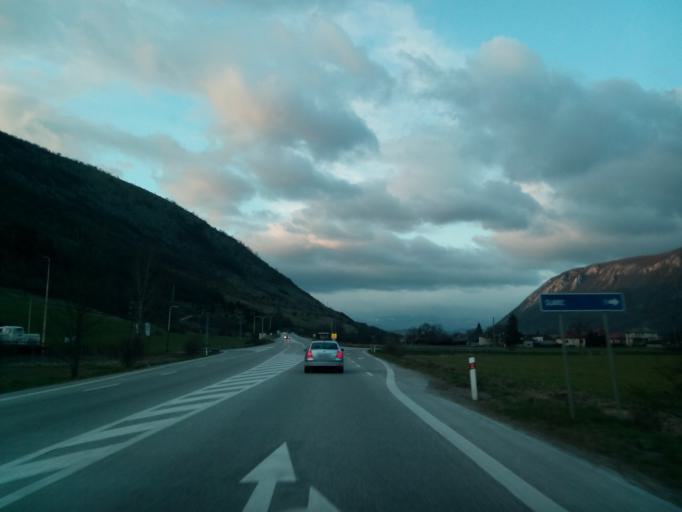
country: SK
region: Kosicky
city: Roznava
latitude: 48.5808
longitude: 20.4635
